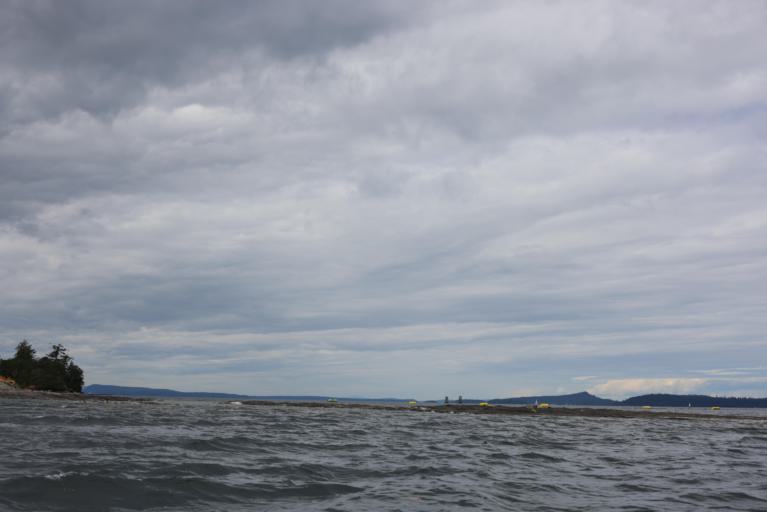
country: CA
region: British Columbia
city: North Cowichan
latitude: 48.8782
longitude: -123.6278
